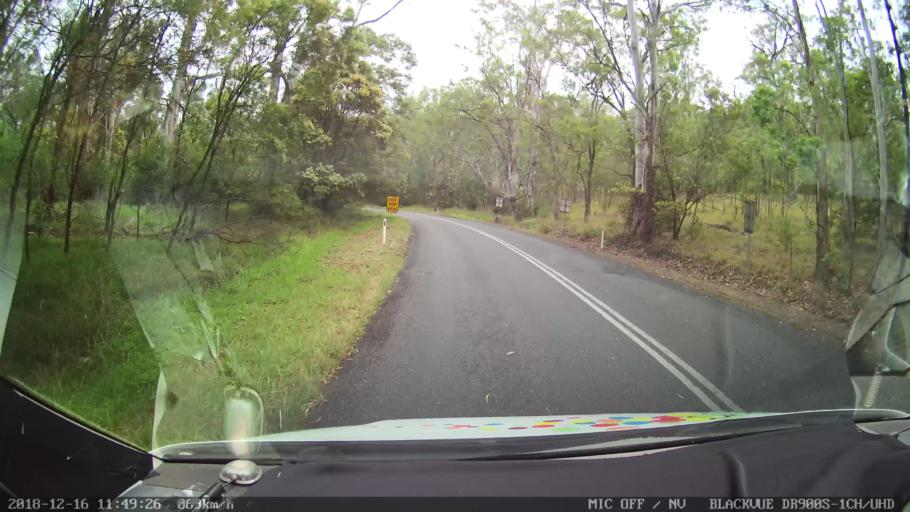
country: AU
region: New South Wales
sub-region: Tenterfield Municipality
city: Carrolls Creek
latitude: -28.9155
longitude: 152.2570
